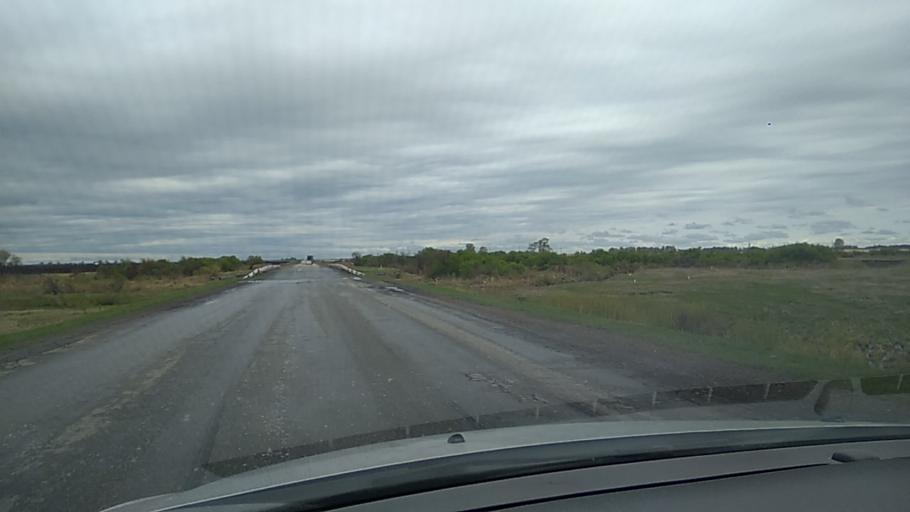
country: RU
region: Kurgan
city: Shatrovo
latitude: 56.4062
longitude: 64.9556
